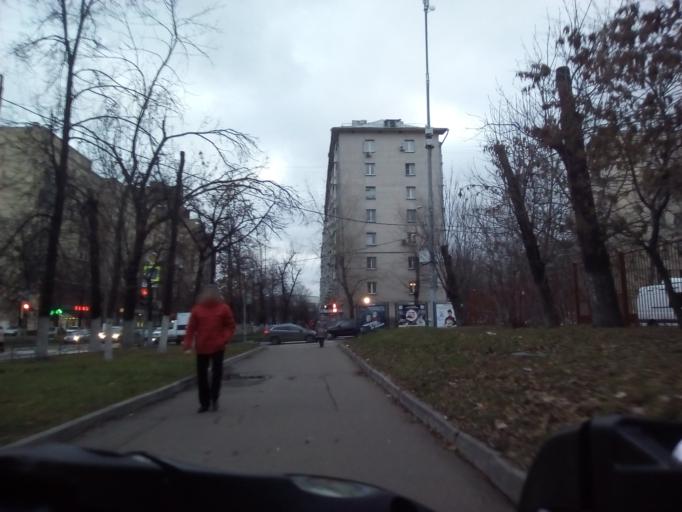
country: RU
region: Moscow
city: Lefortovo
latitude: 55.7475
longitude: 37.7194
